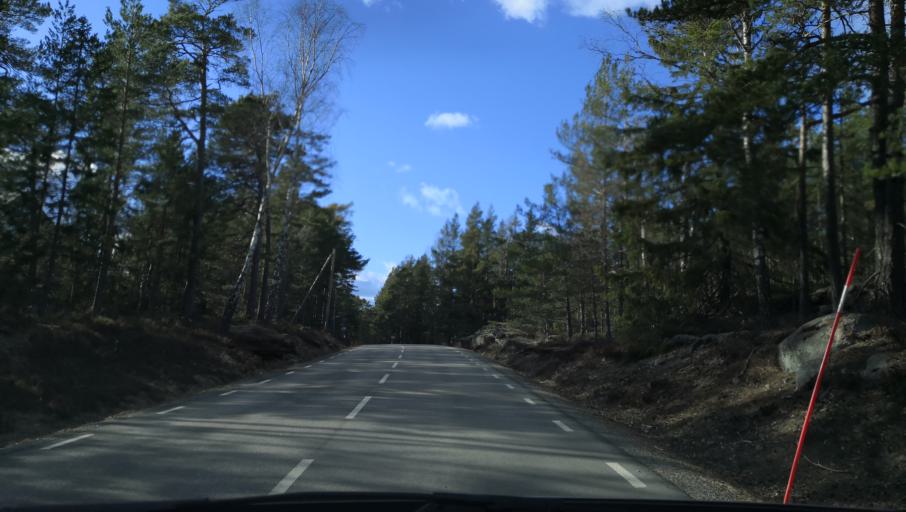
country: SE
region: Stockholm
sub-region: Varmdo Kommun
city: Hemmesta
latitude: 59.2225
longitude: 18.5342
